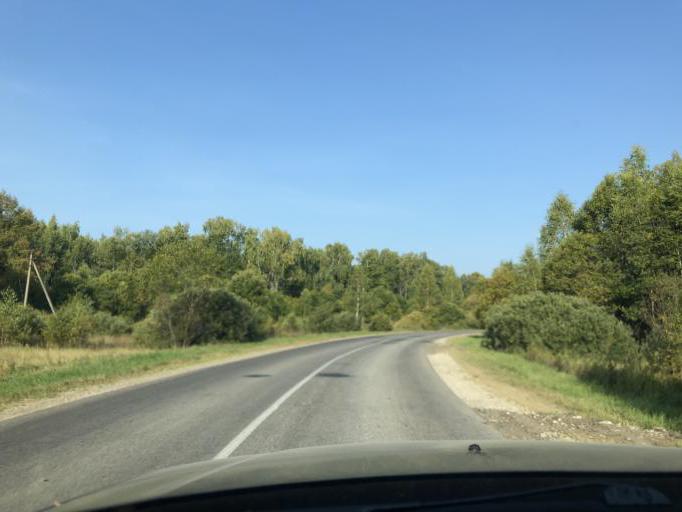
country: RU
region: Tula
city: Leninskiy
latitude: 54.3321
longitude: 37.3857
